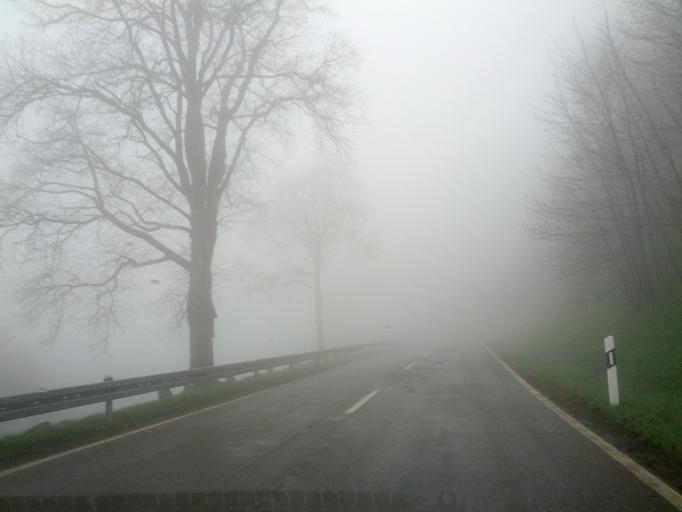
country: DE
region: Baden-Wuerttemberg
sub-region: Freiburg Region
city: Wieden
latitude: 47.8503
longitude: 7.8602
